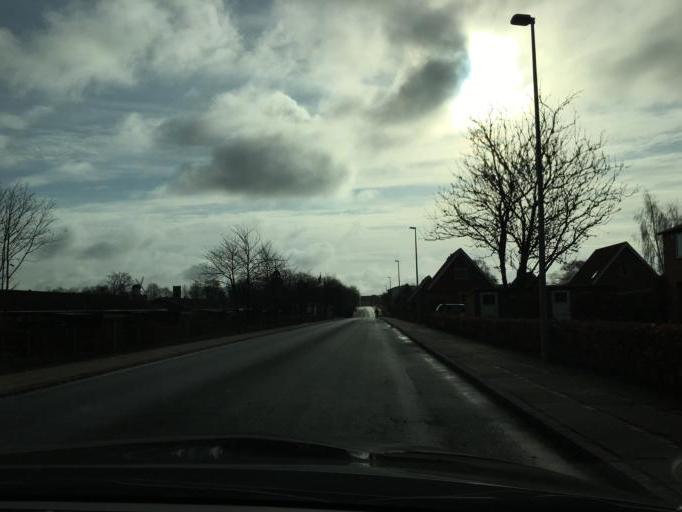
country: DK
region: South Denmark
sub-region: Kolding Kommune
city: Kolding
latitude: 55.4993
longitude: 9.4532
